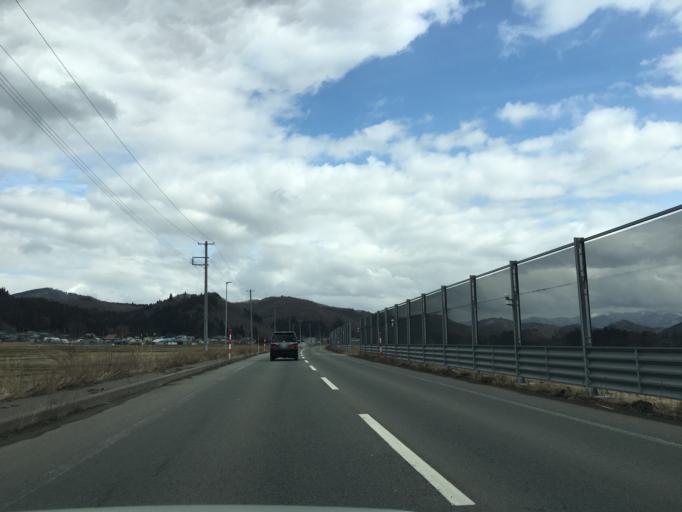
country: JP
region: Akita
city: Hanawa
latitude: 40.2325
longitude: 140.6875
